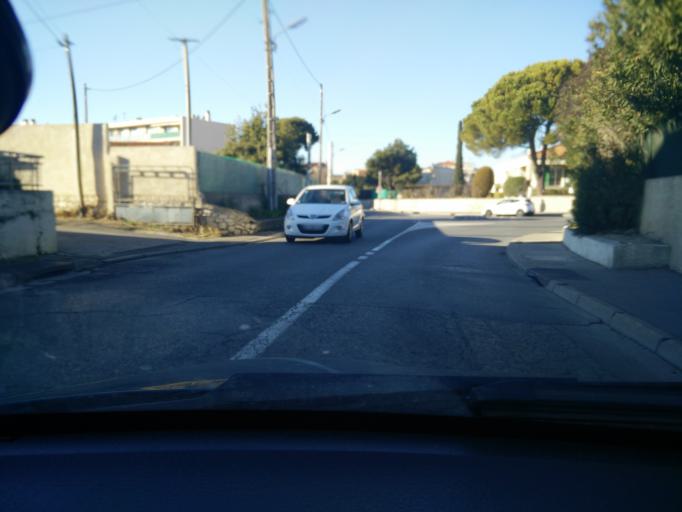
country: FR
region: Provence-Alpes-Cote d'Azur
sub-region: Departement des Bouches-du-Rhone
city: Marignane
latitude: 43.4136
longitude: 5.2166
